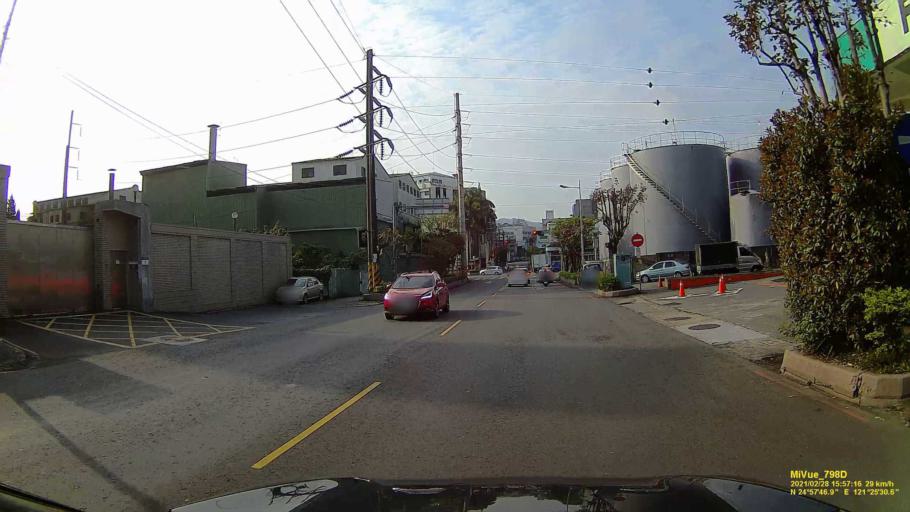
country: TW
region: Taipei
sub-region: Taipei
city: Banqiao
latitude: 24.9631
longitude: 121.4248
